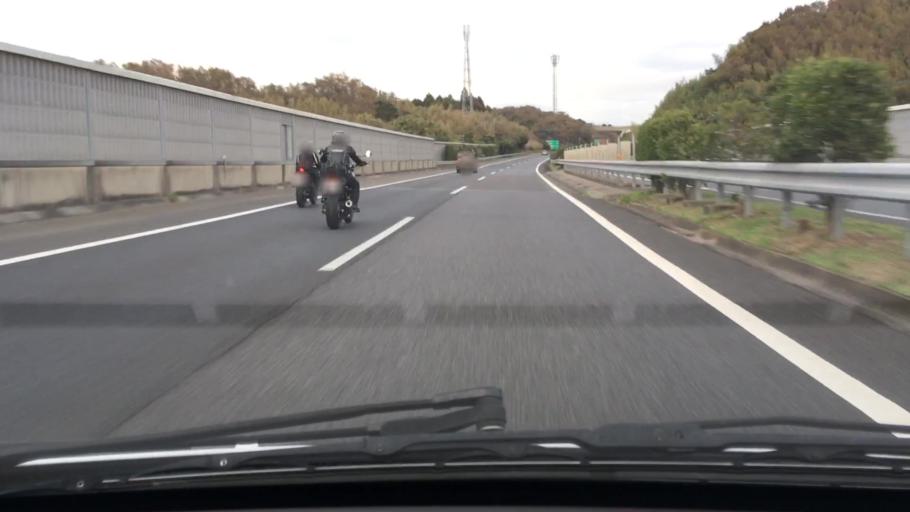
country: JP
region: Chiba
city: Kisarazu
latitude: 35.3636
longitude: 139.9590
